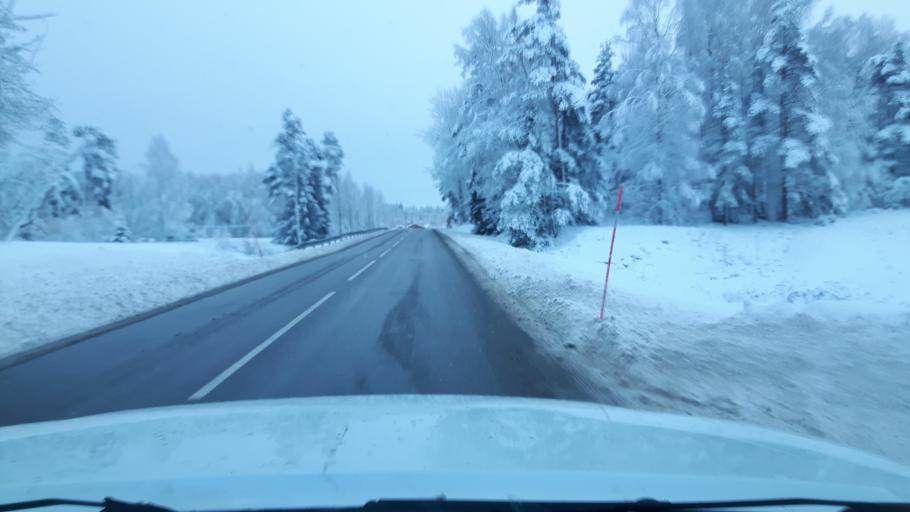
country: SE
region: Halland
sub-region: Kungsbacka Kommun
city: Fjaeras kyrkby
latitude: 57.4104
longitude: 12.2179
